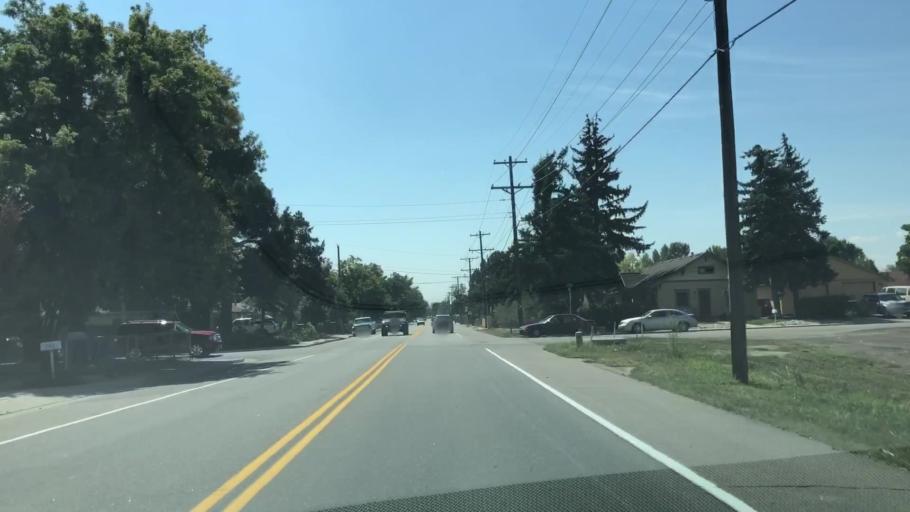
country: US
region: Colorado
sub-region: Larimer County
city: Loveland
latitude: 40.3988
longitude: -105.0589
